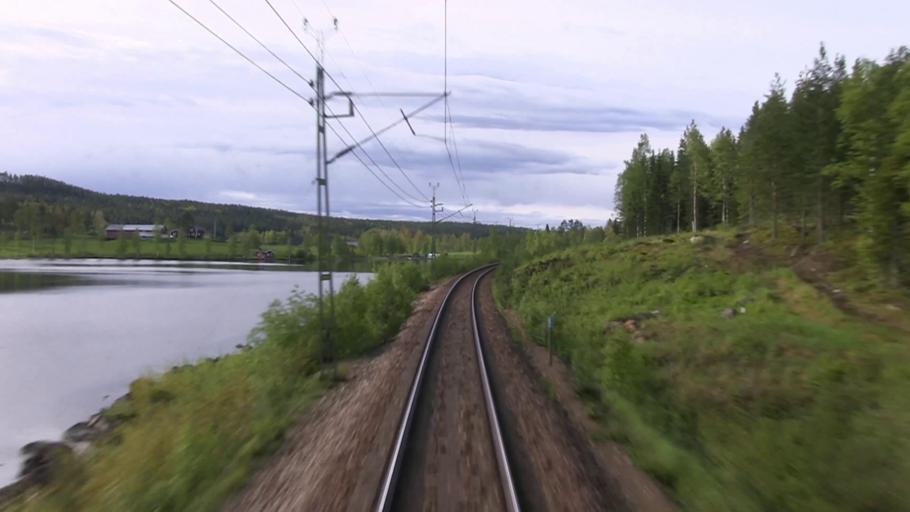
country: SE
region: Vaesterbotten
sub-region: Vindelns Kommun
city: Vindeln
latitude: 64.1132
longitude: 19.6906
